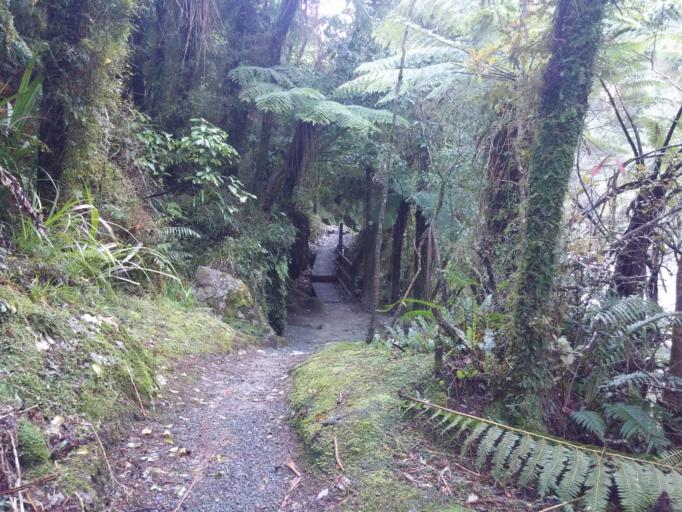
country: NZ
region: West Coast
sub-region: Grey District
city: Greymouth
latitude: -42.1174
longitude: 171.3655
